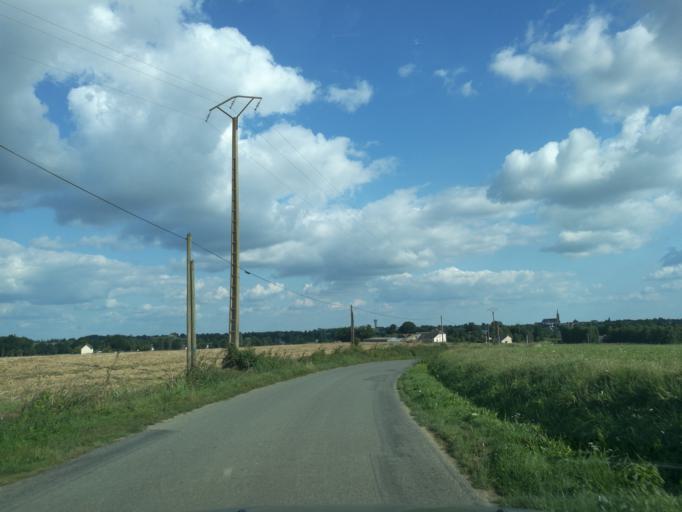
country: FR
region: Brittany
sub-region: Departement d'Ille-et-Vilaine
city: Bedee
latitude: 48.1921
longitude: -1.9601
